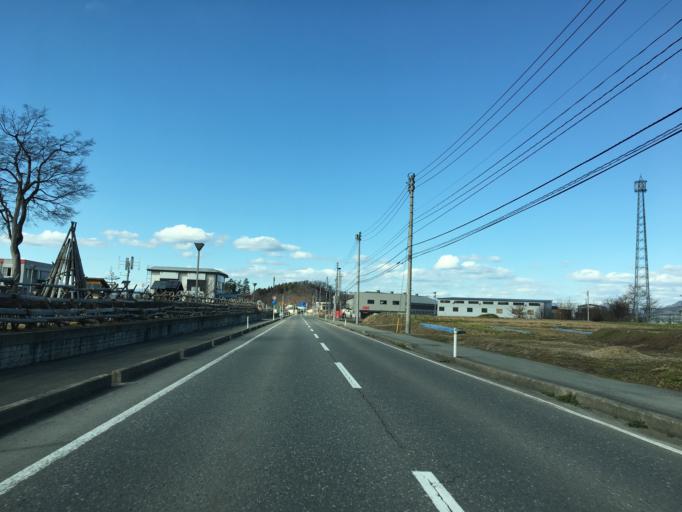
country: JP
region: Yamagata
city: Yonezawa
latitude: 37.9167
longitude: 140.1460
